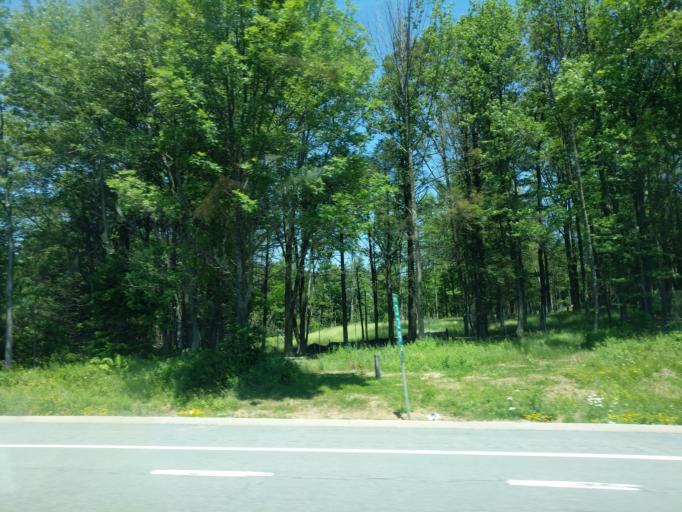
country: US
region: New York
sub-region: Sullivan County
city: Monticello
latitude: 41.6458
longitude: -74.6505
